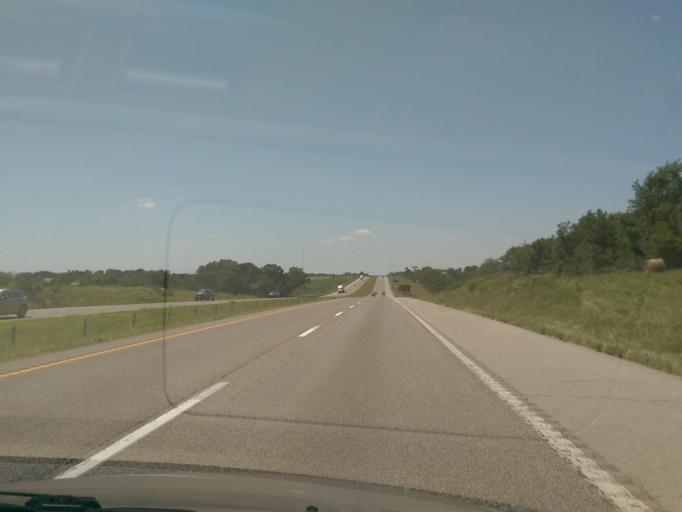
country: US
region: Missouri
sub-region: Saline County
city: Marshall
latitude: 38.9522
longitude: -93.0724
